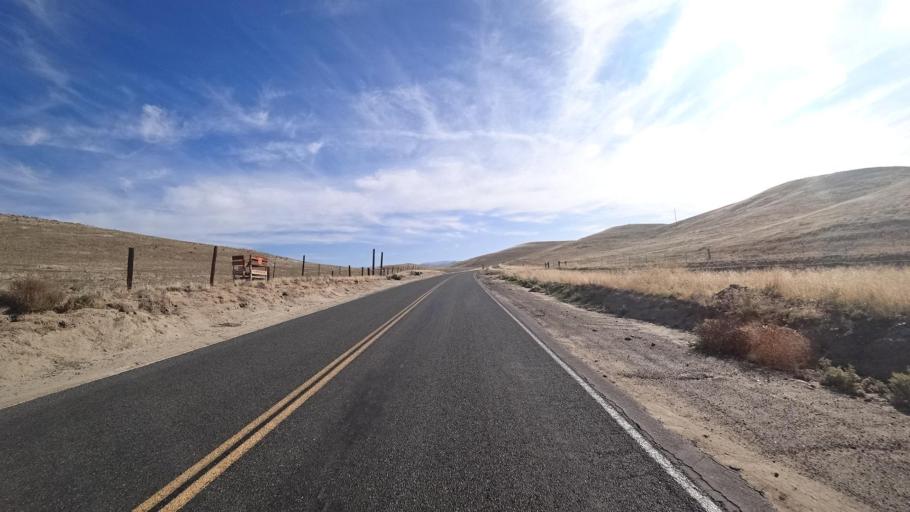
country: US
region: California
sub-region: Kern County
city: Oildale
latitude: 35.6106
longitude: -118.9184
